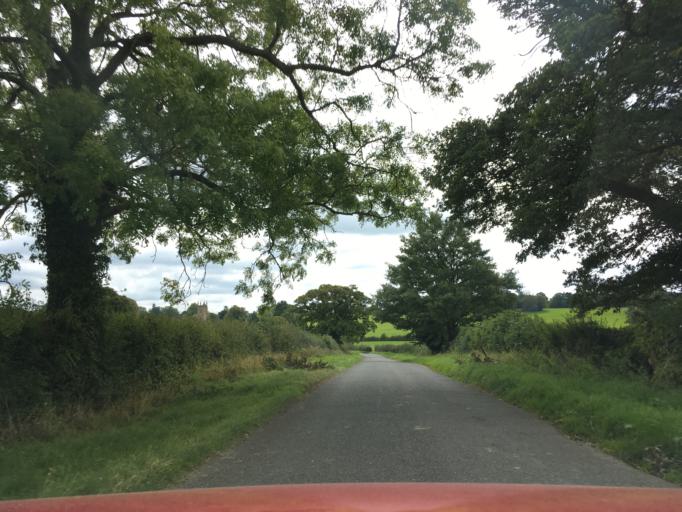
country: GB
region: England
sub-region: South Gloucestershire
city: Charfield
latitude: 51.6425
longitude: -2.4308
